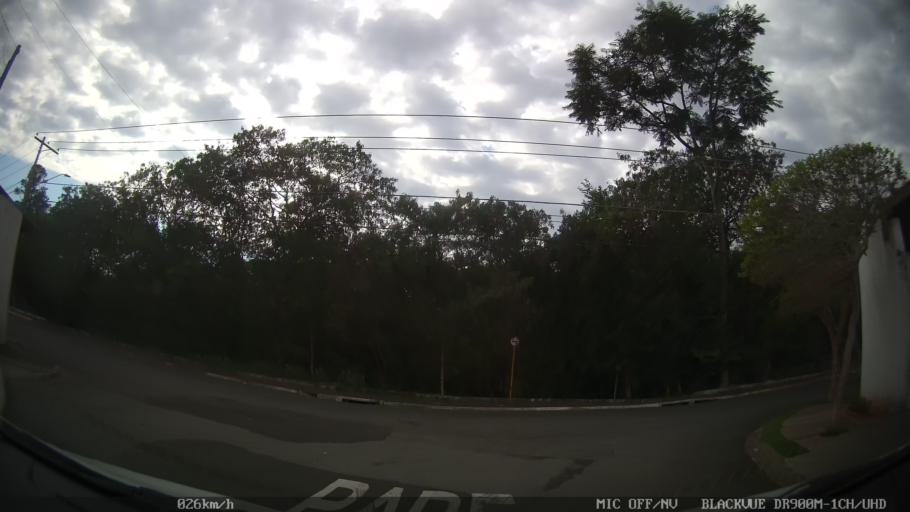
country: BR
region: Sao Paulo
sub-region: Americana
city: Americana
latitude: -22.7243
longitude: -47.3545
